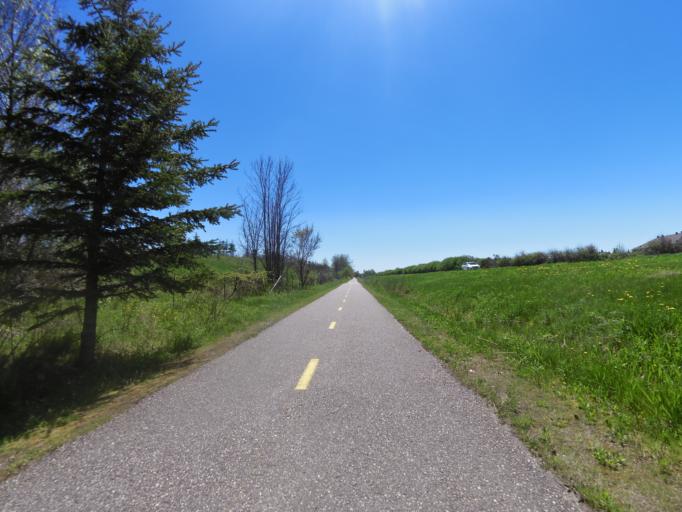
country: CA
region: Ontario
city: Ottawa
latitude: 45.4252
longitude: -75.7997
